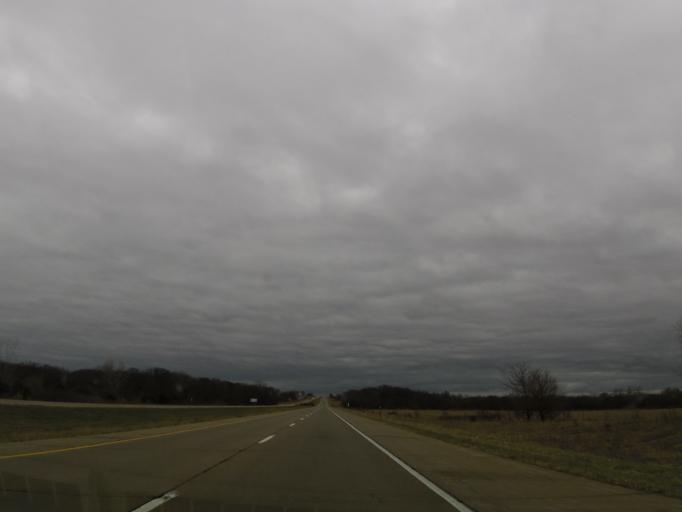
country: US
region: Iowa
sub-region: Benton County
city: Urbana
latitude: 42.3025
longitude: -91.9663
